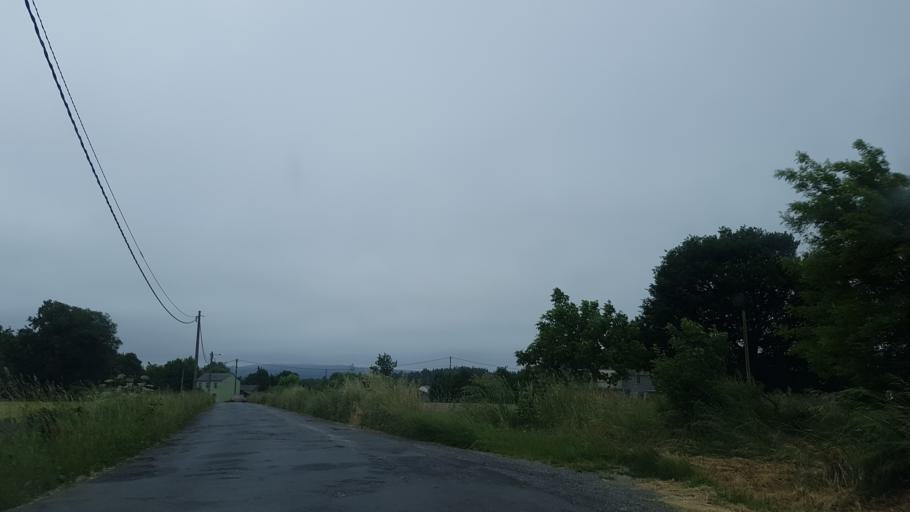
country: ES
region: Galicia
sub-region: Provincia de Lugo
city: Lugo
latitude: 43.0476
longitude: -7.5792
